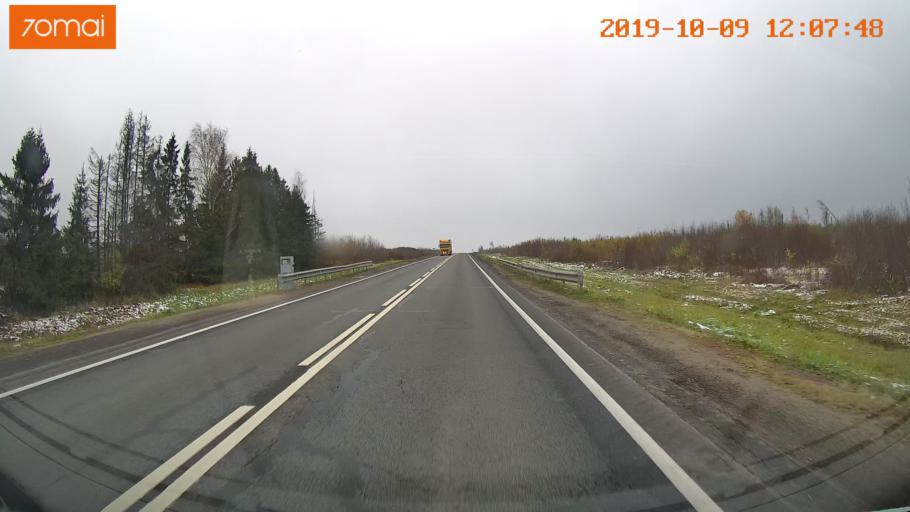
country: RU
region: Jaroslavl
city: Prechistoye
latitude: 58.5948
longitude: 40.3439
